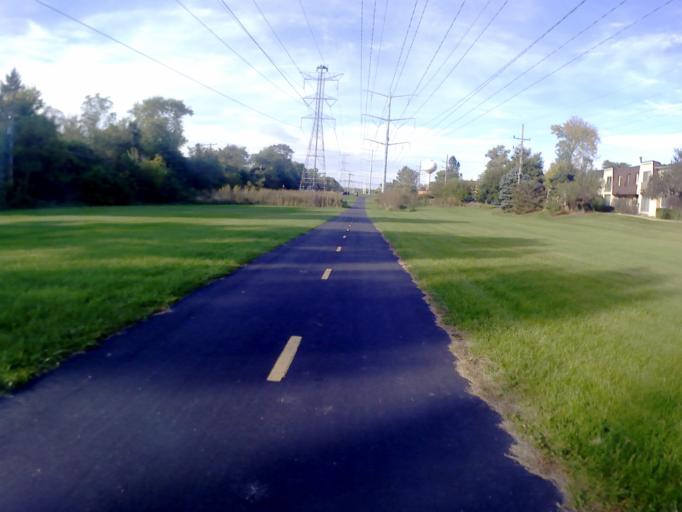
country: US
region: Illinois
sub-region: DuPage County
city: Woodridge
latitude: 41.7614
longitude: -88.0597
